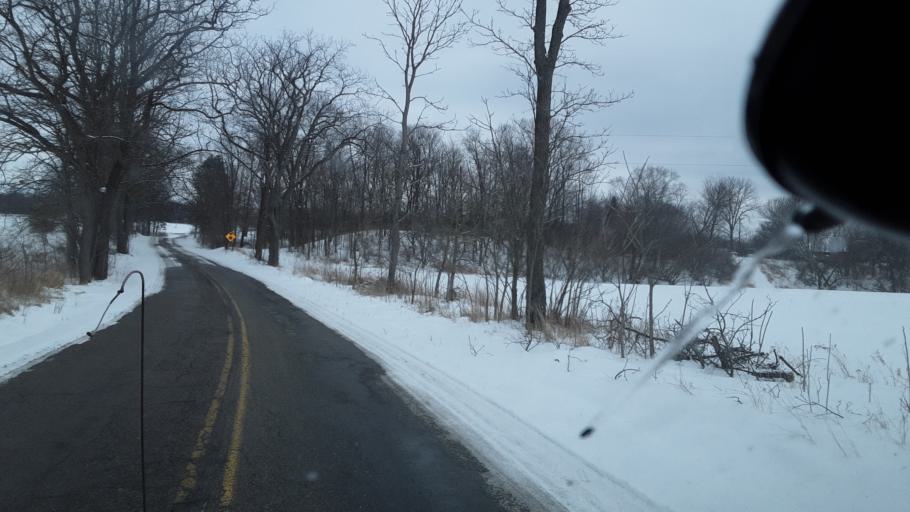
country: US
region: Michigan
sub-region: Ingham County
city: Mason
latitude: 42.5333
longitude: -84.3919
